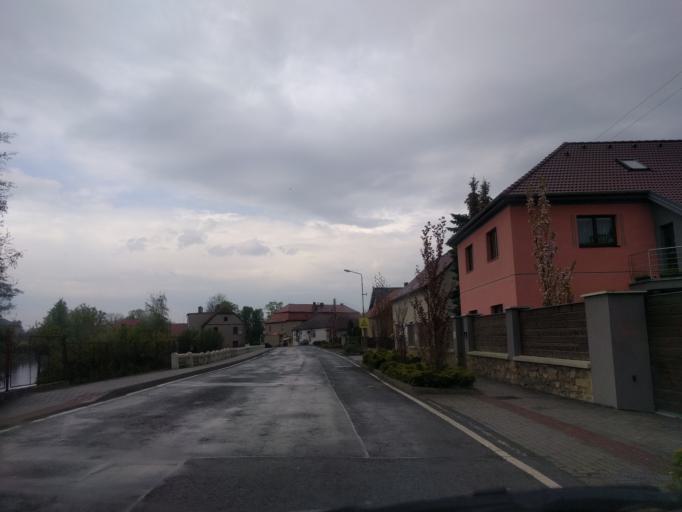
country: CZ
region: Central Bohemia
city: Dobris
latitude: 49.7408
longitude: 14.1514
